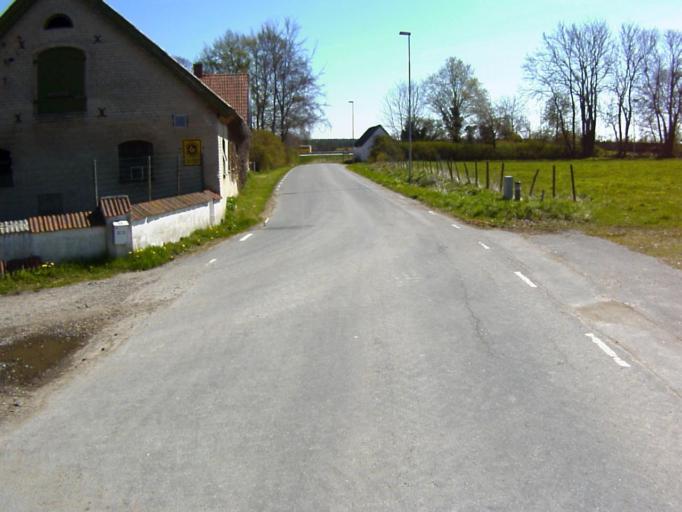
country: SE
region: Skane
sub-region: Kristianstads Kommun
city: Norra Asum
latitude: 55.9923
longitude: 14.0908
